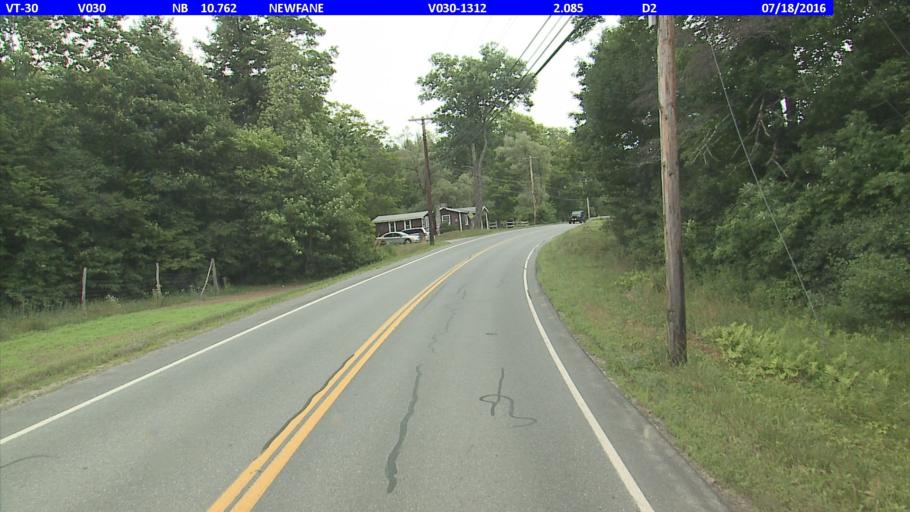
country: US
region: Vermont
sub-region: Windham County
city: Newfane
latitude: 42.9742
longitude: -72.6583
